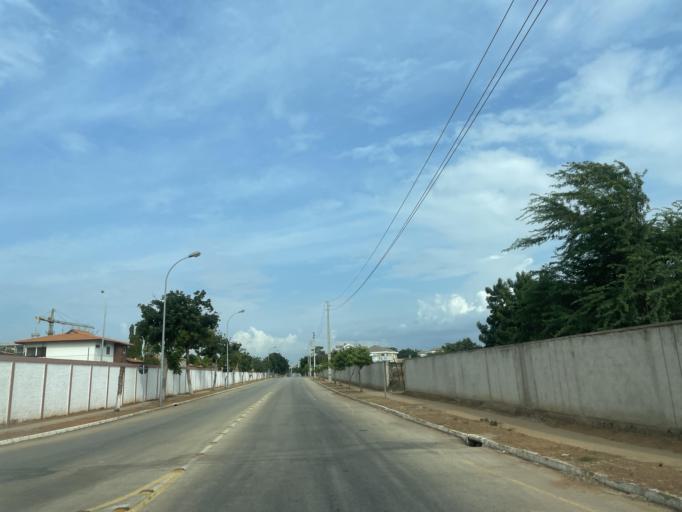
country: AO
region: Luanda
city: Luanda
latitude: -8.9305
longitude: 13.1797
